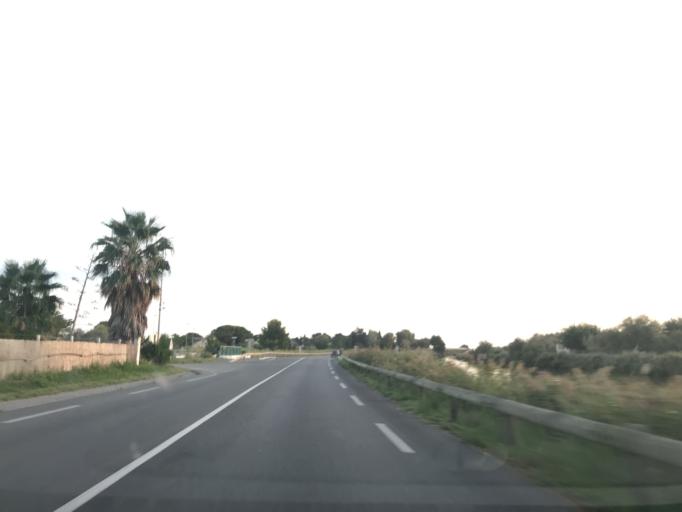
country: FR
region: Languedoc-Roussillon
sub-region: Departement du Gard
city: Aigues-Mortes
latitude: 43.5618
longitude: 4.1852
